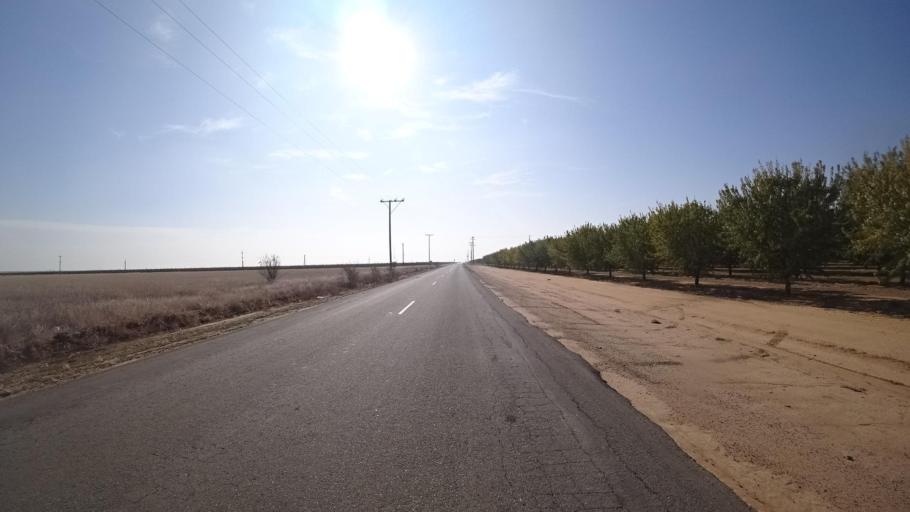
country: US
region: California
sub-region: Kern County
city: McFarland
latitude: 35.6617
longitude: -119.1691
